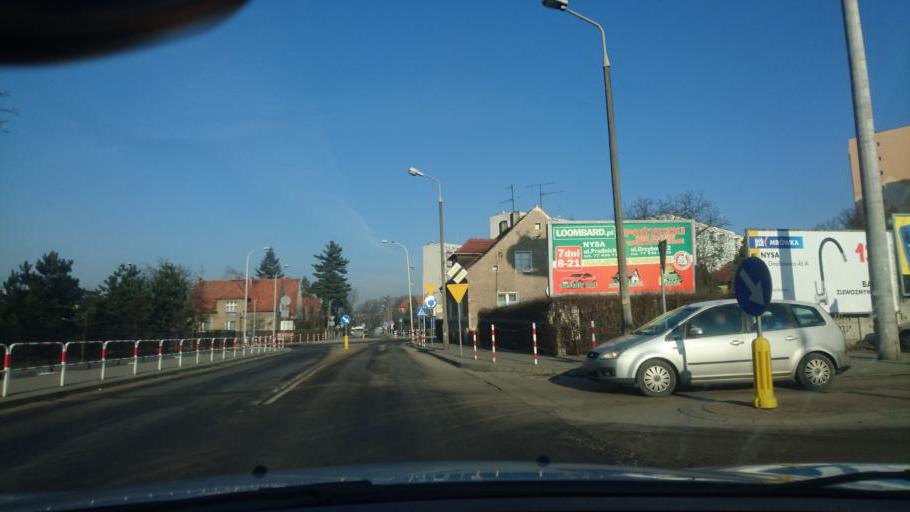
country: PL
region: Opole Voivodeship
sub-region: Powiat nyski
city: Nysa
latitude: 50.4643
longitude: 17.3396
